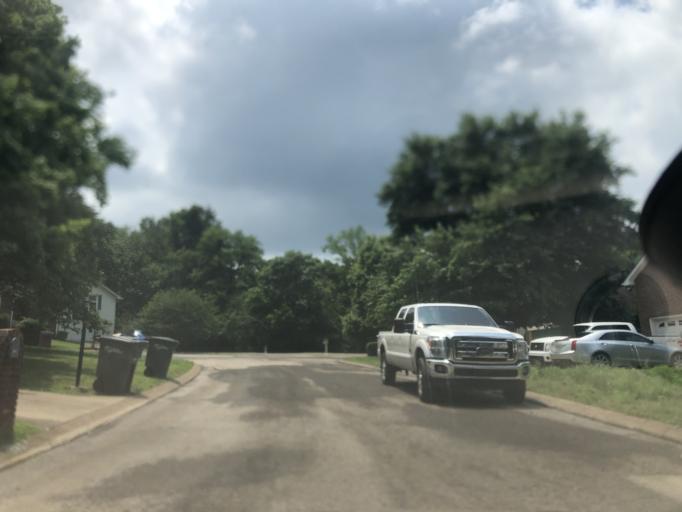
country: US
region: Tennessee
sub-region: Davidson County
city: Lakewood
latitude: 36.2158
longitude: -86.6299
